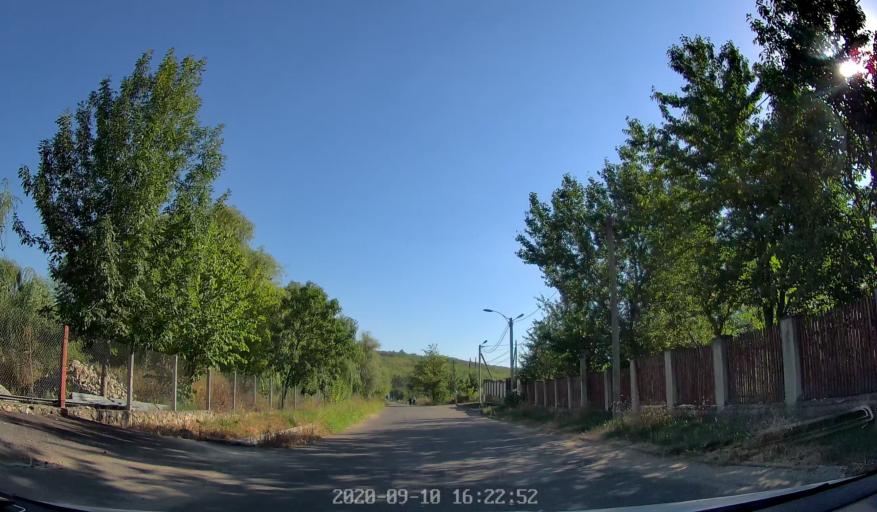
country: MD
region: Chisinau
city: Stauceni
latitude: 47.0511
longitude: 28.9253
